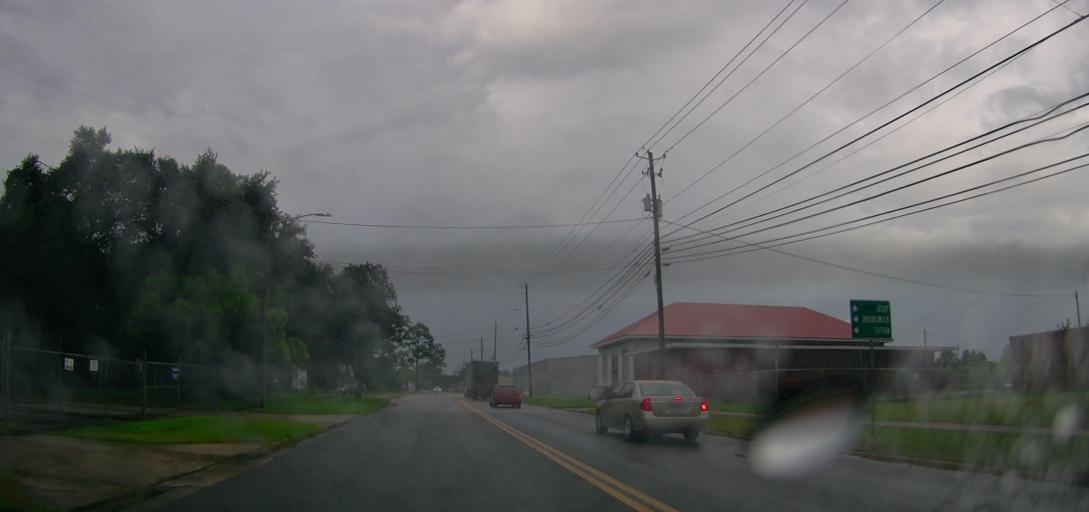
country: US
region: Georgia
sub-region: Ware County
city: Waycross
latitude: 31.2079
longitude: -82.3650
